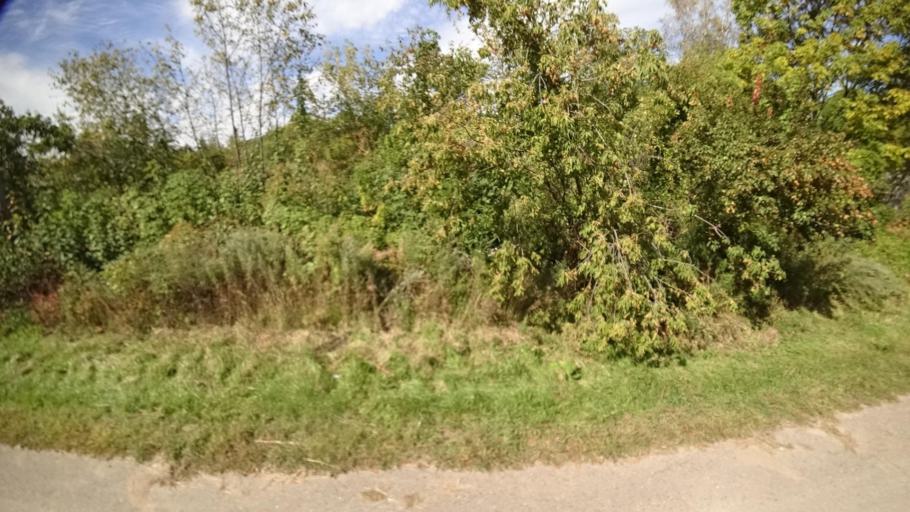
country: RU
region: Primorskiy
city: Yakovlevka
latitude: 44.6561
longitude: 133.7447
